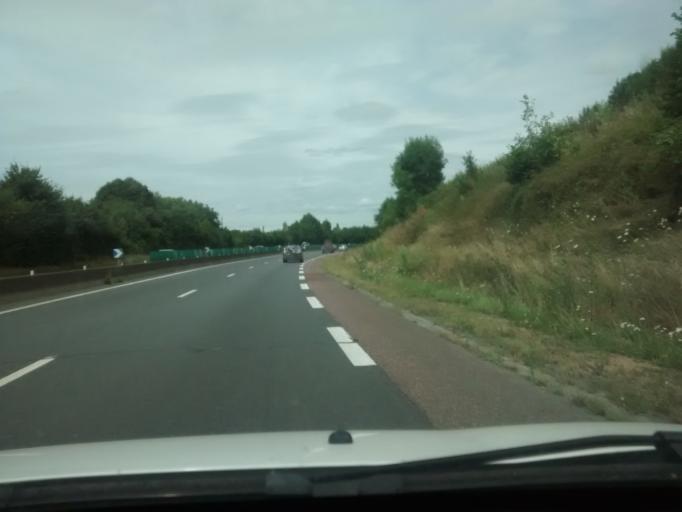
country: FR
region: Lower Normandy
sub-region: Departement de la Manche
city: Avranches
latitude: 48.6839
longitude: -1.3741
